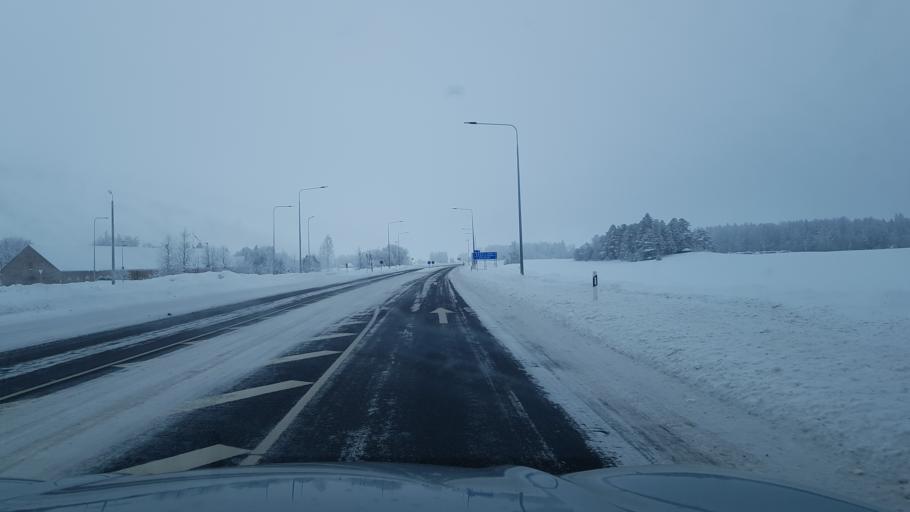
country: EE
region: Ida-Virumaa
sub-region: Johvi vald
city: Johvi
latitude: 59.2260
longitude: 27.3382
